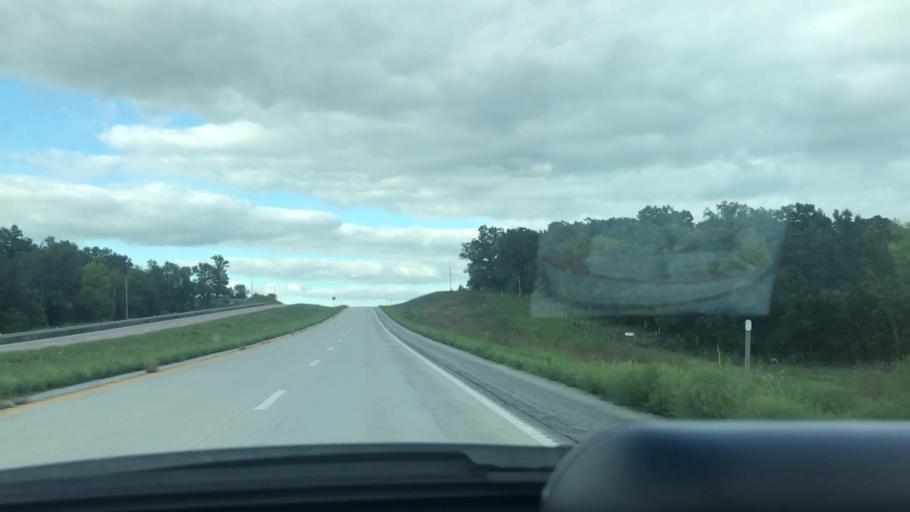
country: US
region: Missouri
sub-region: Benton County
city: Lincoln
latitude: 38.4388
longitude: -93.2992
